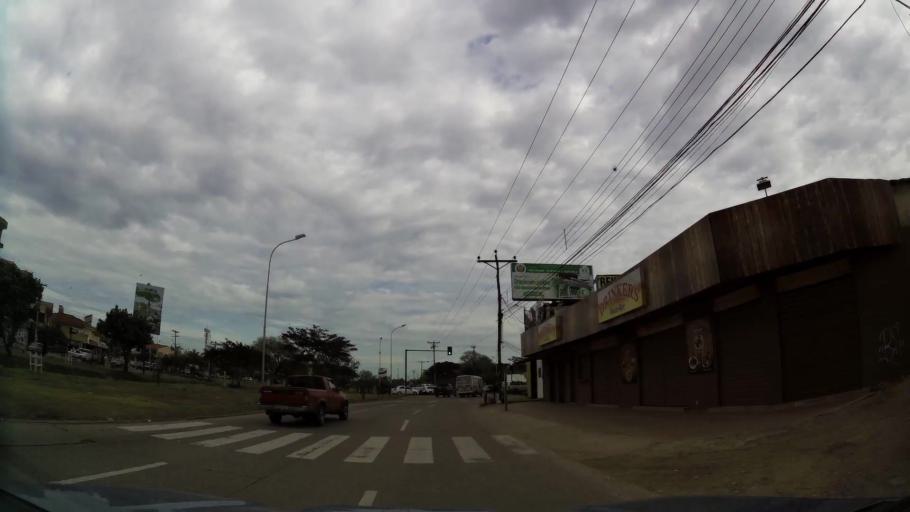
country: BO
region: Santa Cruz
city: Santa Cruz de la Sierra
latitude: -17.7494
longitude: -63.1797
